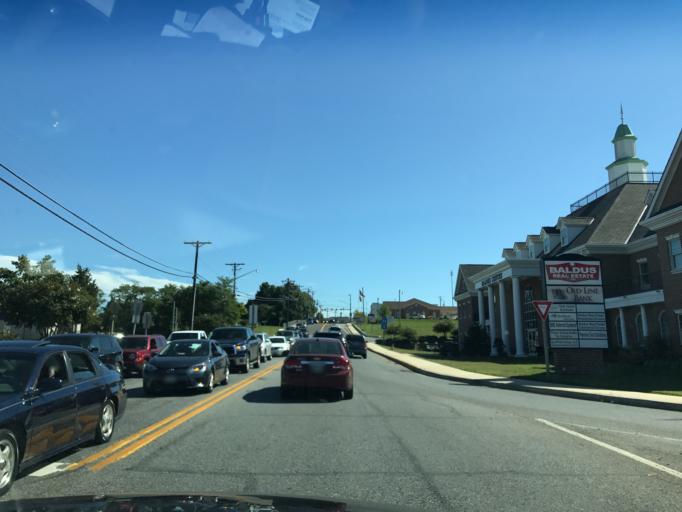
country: US
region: Maryland
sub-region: Charles County
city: La Plata
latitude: 38.5291
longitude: -76.9827
